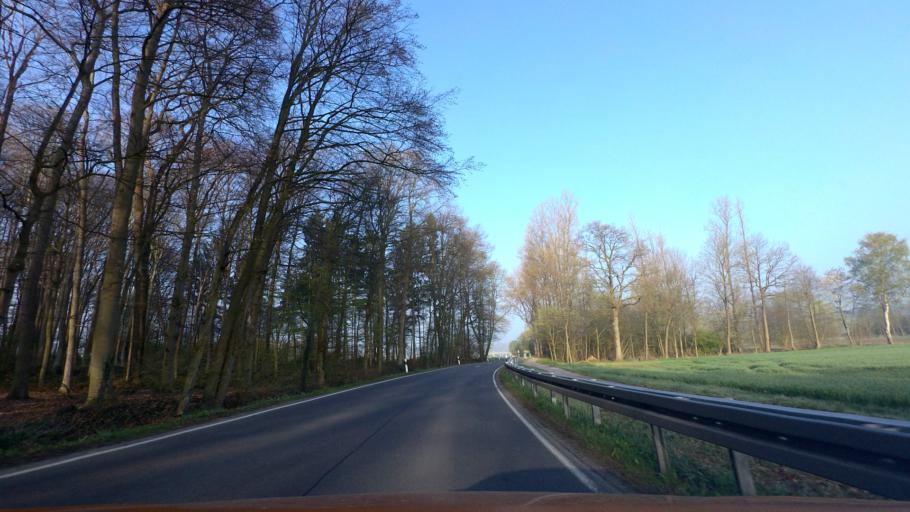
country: DE
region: Lower Saxony
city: Neuenkirchen
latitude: 52.1835
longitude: 8.3903
